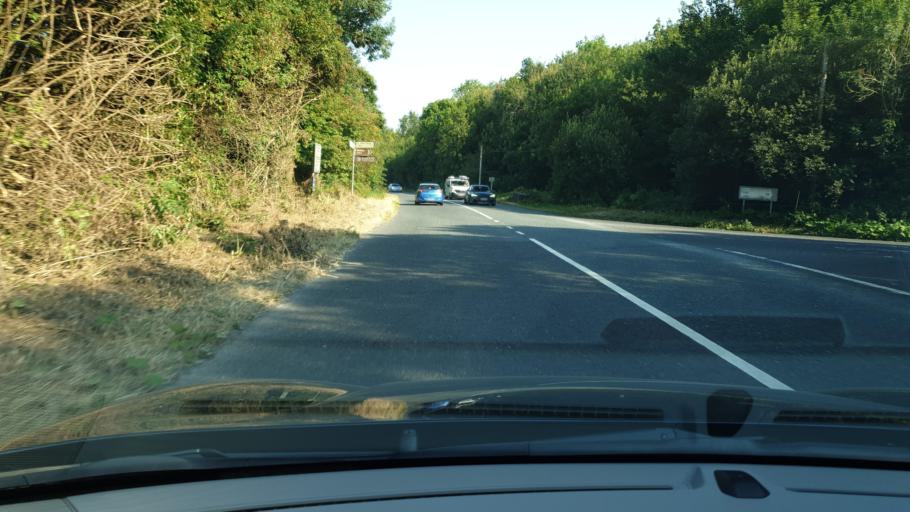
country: IE
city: Kentstown
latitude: 53.6235
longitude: -6.5189
